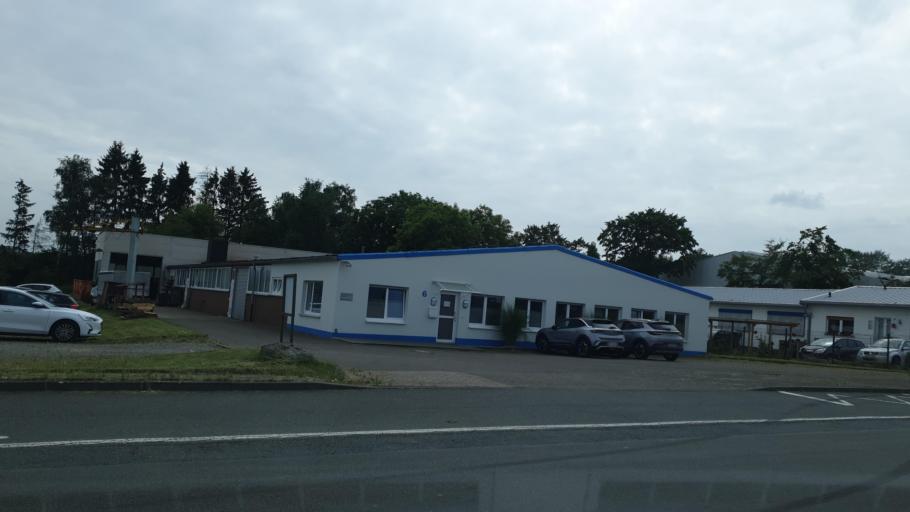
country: DE
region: North Rhine-Westphalia
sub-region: Regierungsbezirk Detmold
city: Bad Salzuflen
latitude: 52.1296
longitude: 8.7921
